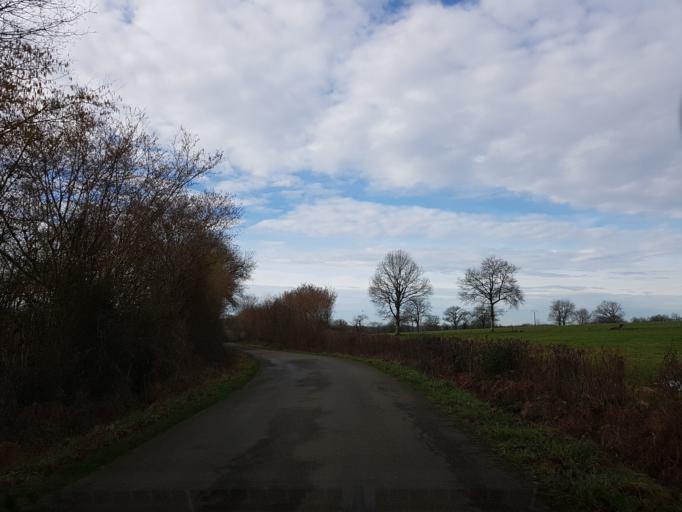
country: FR
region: Poitou-Charentes
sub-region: Departement de la Charente
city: Brigueuil
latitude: 45.9909
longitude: 0.8345
